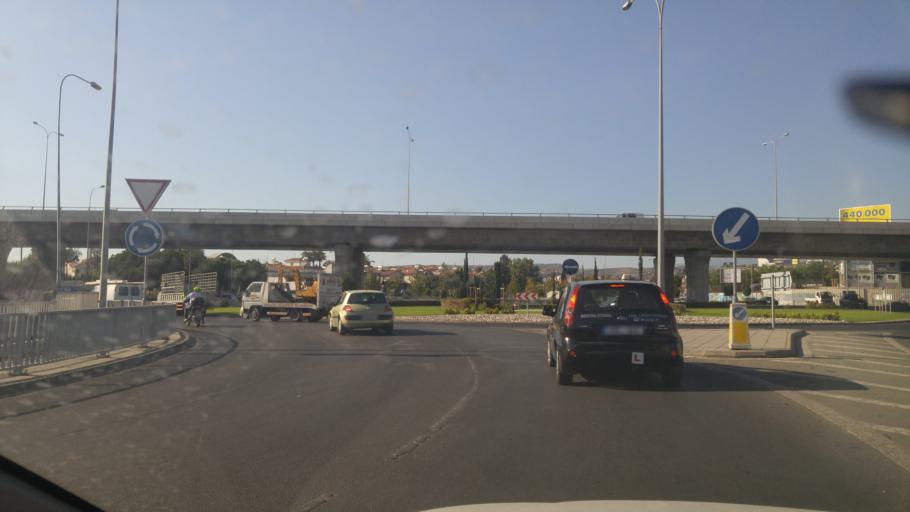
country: CY
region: Limassol
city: Pano Polemidia
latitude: 34.6937
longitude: 33.0144
